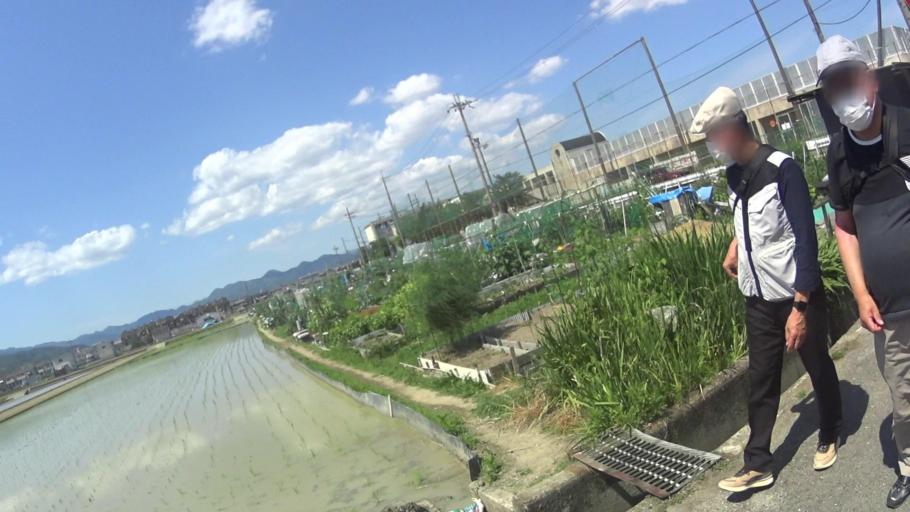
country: JP
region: Kyoto
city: Muko
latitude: 34.9661
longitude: 135.6959
